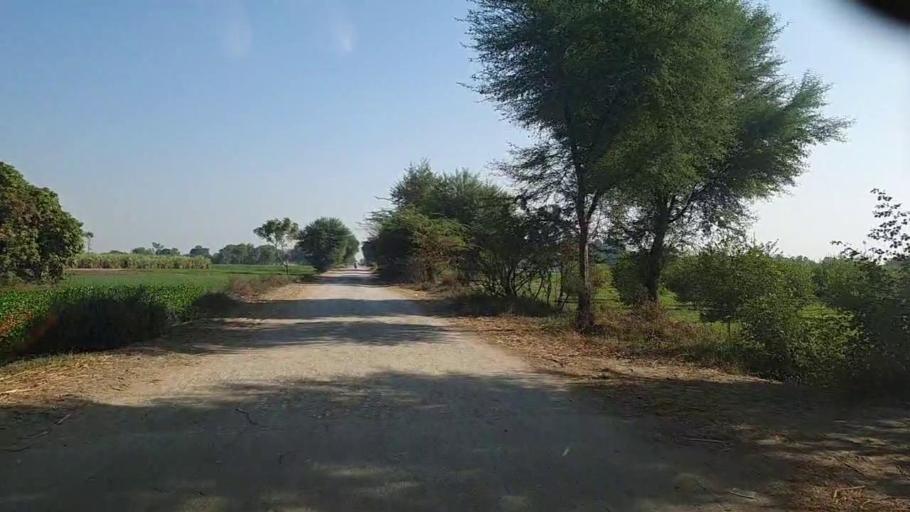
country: PK
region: Sindh
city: Darya Khan Marri
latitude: 26.6608
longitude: 68.3429
